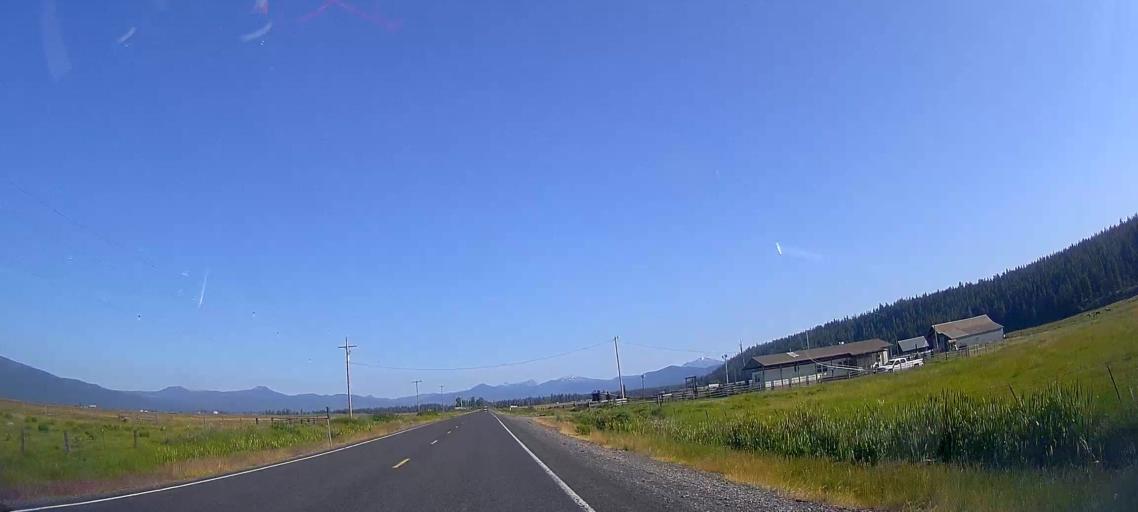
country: US
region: Oregon
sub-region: Klamath County
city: Klamath Falls
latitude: 42.6525
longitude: -121.9574
